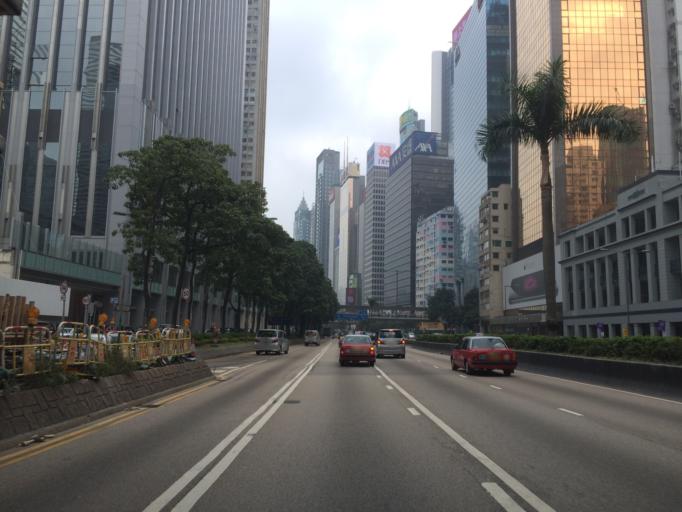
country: HK
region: Wanchai
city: Wan Chai
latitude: 22.2796
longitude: 114.1746
